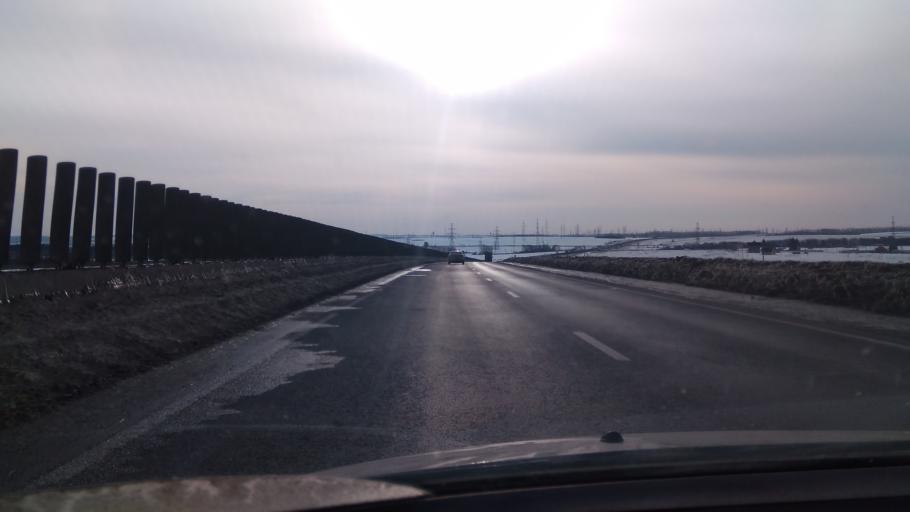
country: RU
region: Perm
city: Ferma
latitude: 57.9346
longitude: 56.3550
